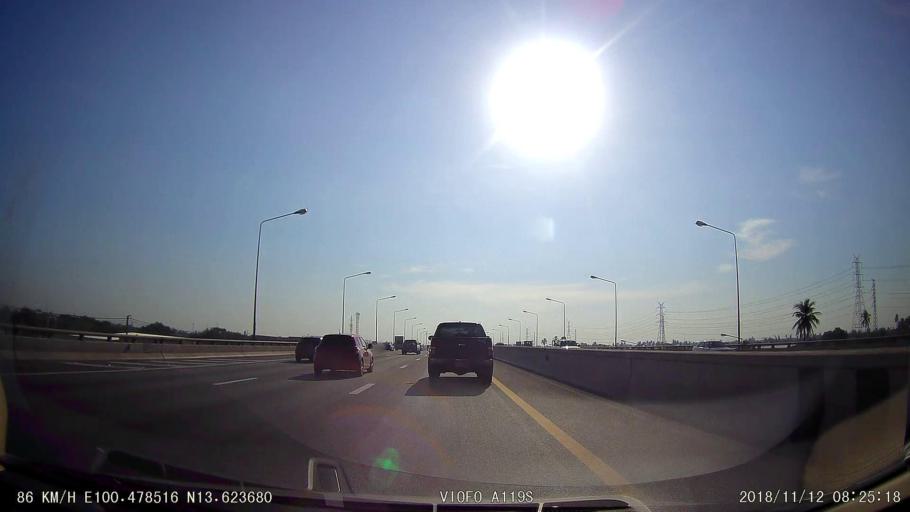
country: TH
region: Bangkok
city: Thung Khru
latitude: 13.6236
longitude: 100.4789
